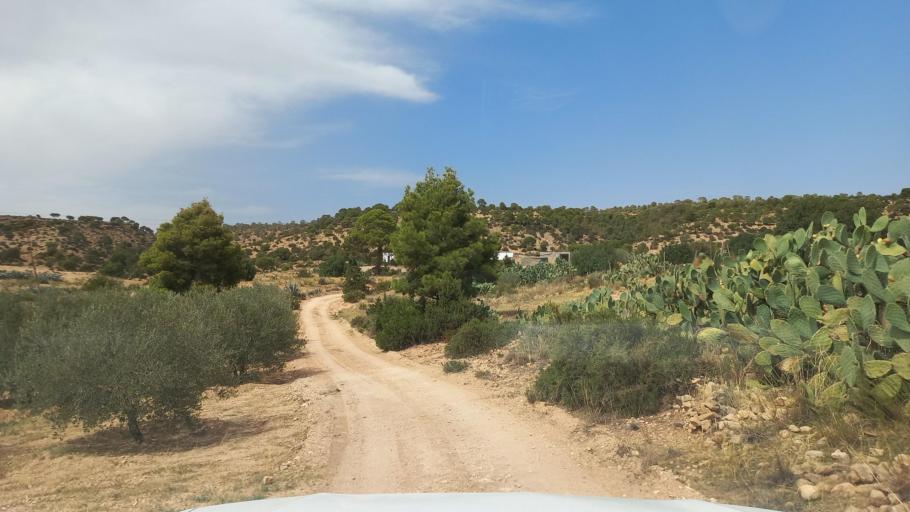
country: TN
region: Al Qasrayn
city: Kasserine
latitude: 35.3720
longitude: 8.8916
